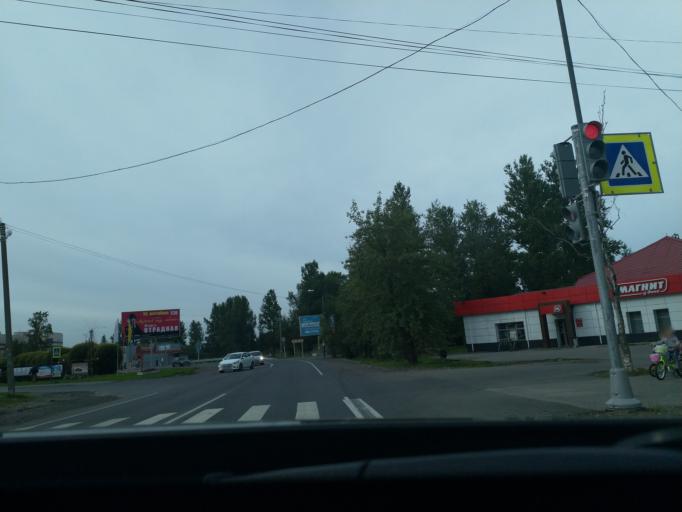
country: RU
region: Leningrad
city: Nikol'skoye
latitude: 59.7073
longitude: 30.7843
